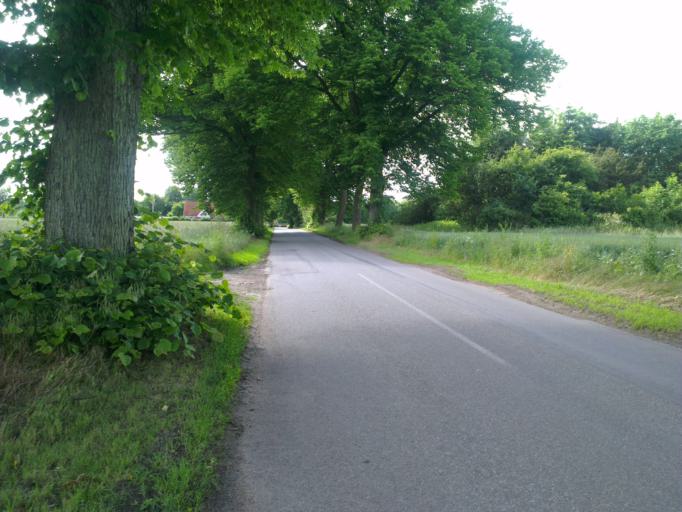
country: DK
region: Capital Region
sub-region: Frederikssund Kommune
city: Skibby
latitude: 55.7263
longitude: 11.9567
